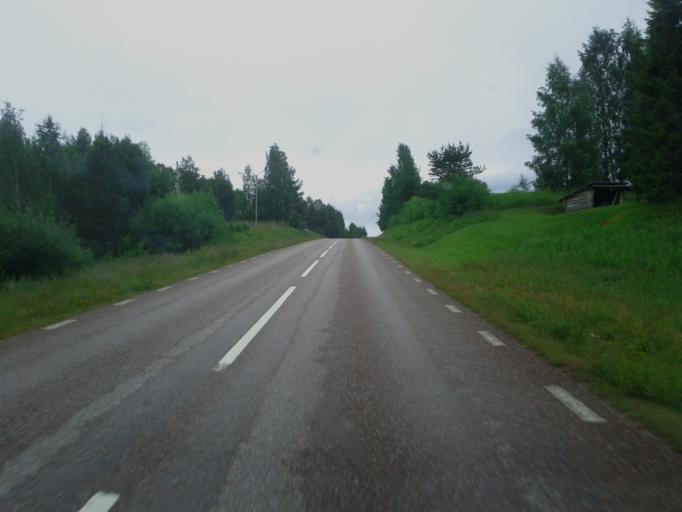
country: NO
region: Hedmark
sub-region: Trysil
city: Innbygda
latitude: 61.7335
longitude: 12.9842
